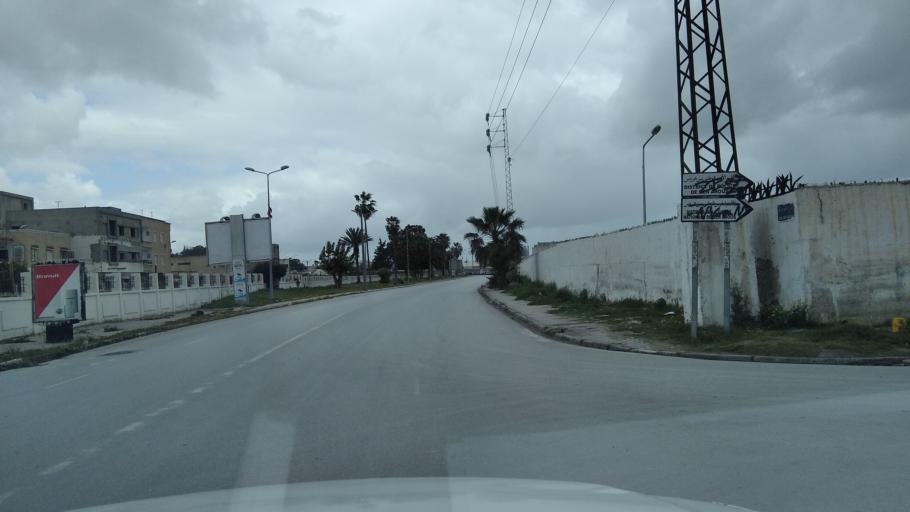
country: TN
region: Bin 'Arus
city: Ben Arous
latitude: 36.7574
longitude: 10.2187
